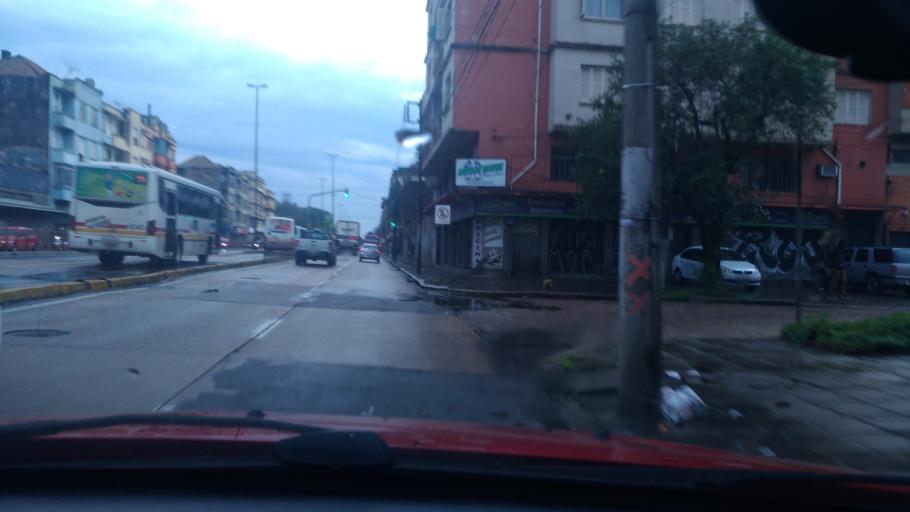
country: BR
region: Rio Grande do Sul
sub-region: Porto Alegre
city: Porto Alegre
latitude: -30.0081
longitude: -51.2016
